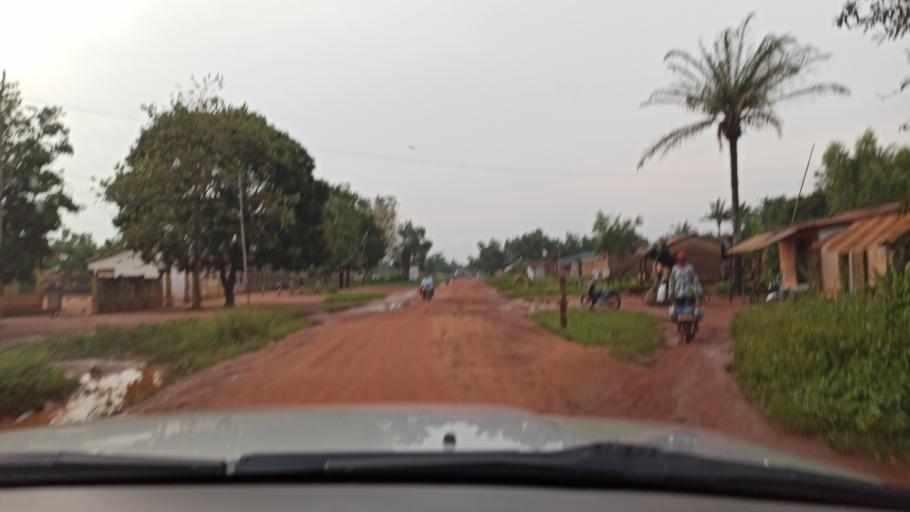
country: BJ
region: Queme
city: Porto-Novo
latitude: 6.5451
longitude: 2.6170
